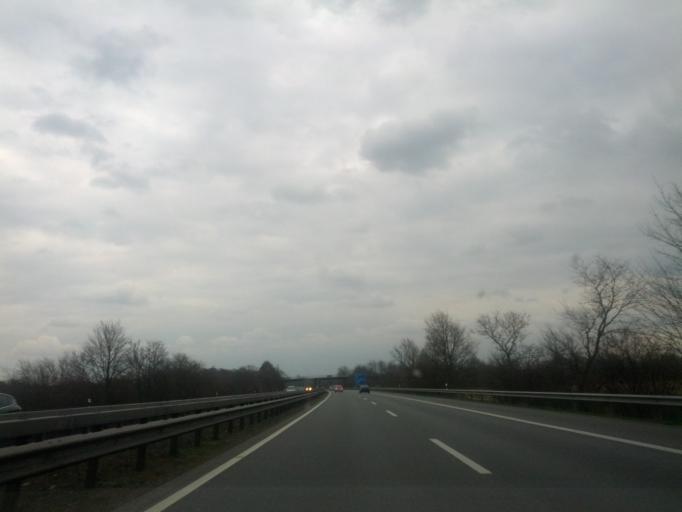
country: DE
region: Lower Saxony
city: Hatten
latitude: 53.0680
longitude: 8.3360
